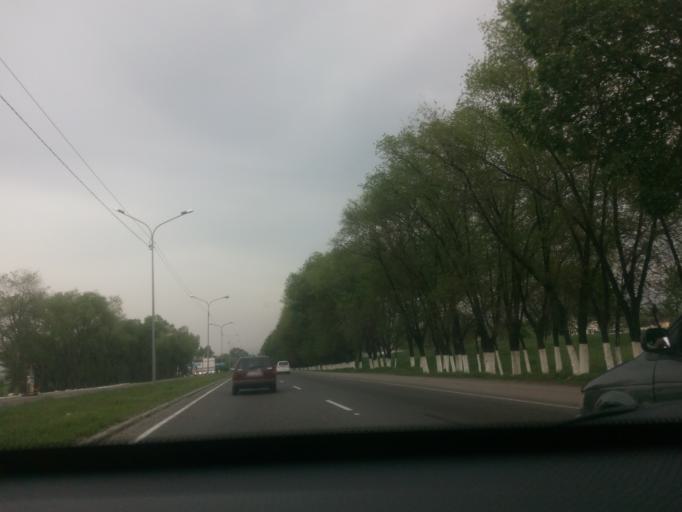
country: KZ
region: Almaty Oblysy
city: Burunday
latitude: 43.2252
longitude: 76.7290
